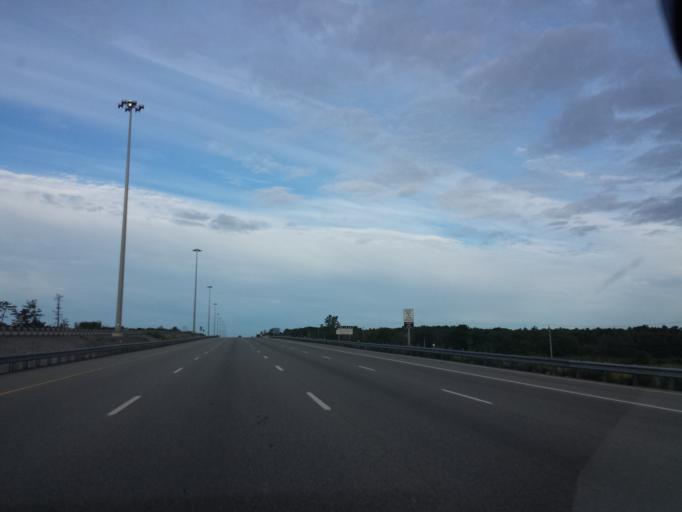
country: CA
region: Ontario
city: Bells Corners
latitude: 45.3337
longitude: -75.8535
